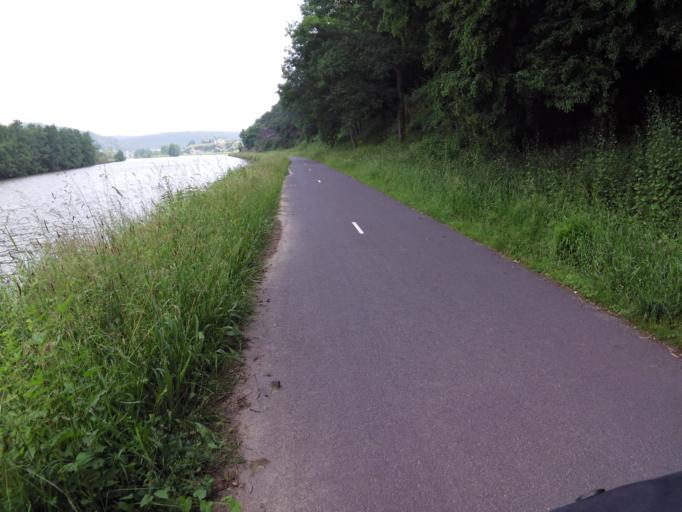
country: FR
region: Champagne-Ardenne
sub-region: Departement des Ardennes
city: Vireux-Molhain
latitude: 50.0745
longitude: 4.7286
